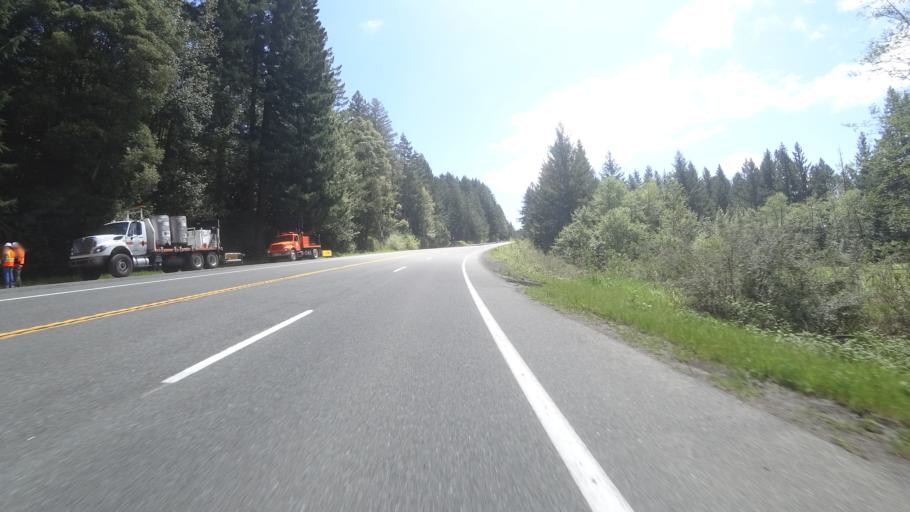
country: US
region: California
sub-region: Humboldt County
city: Blue Lake
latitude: 40.9446
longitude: -123.8747
